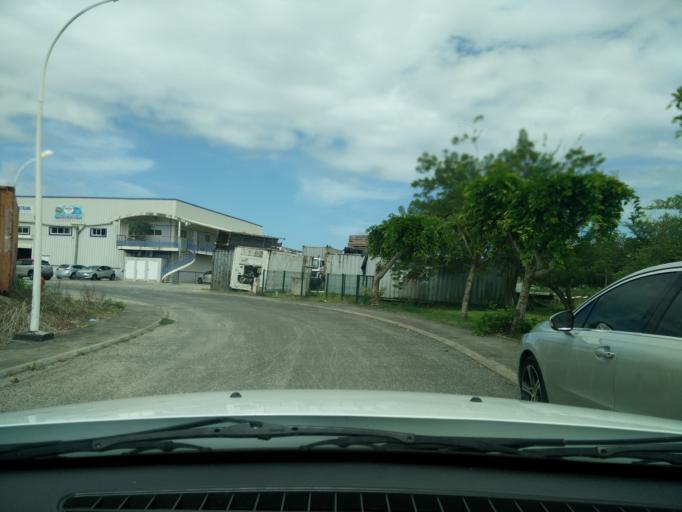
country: GP
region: Guadeloupe
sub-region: Guadeloupe
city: Petit-Bourg
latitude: 16.2000
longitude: -61.6079
